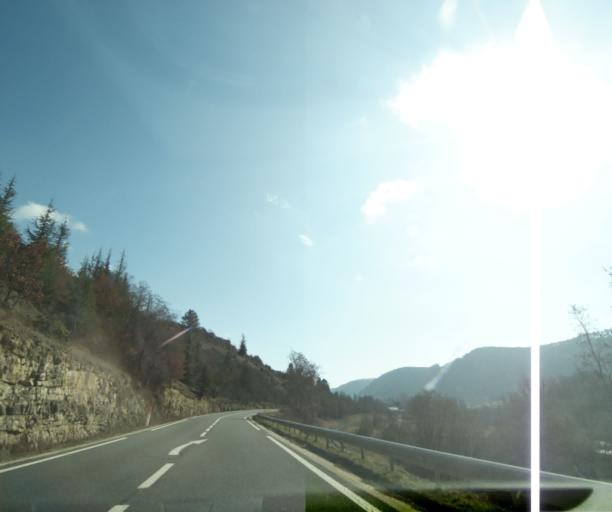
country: FR
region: Languedoc-Roussillon
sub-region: Departement de la Lozere
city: Chanac
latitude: 44.4837
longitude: 3.3126
